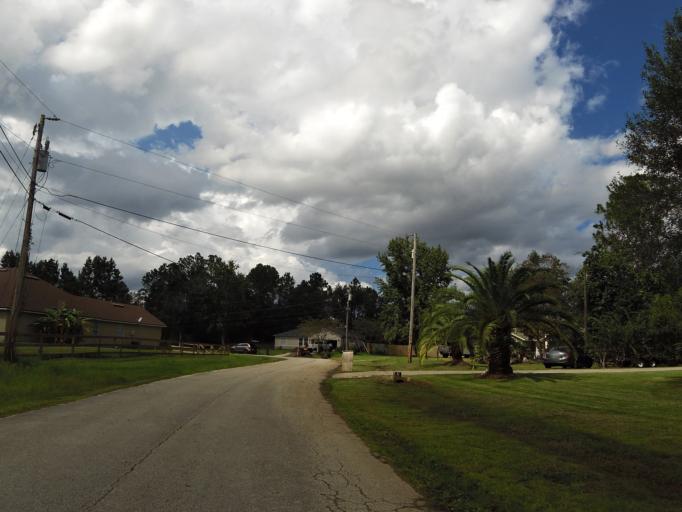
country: US
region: Florida
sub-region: Saint Johns County
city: Saint Augustine
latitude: 29.9196
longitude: -81.4992
